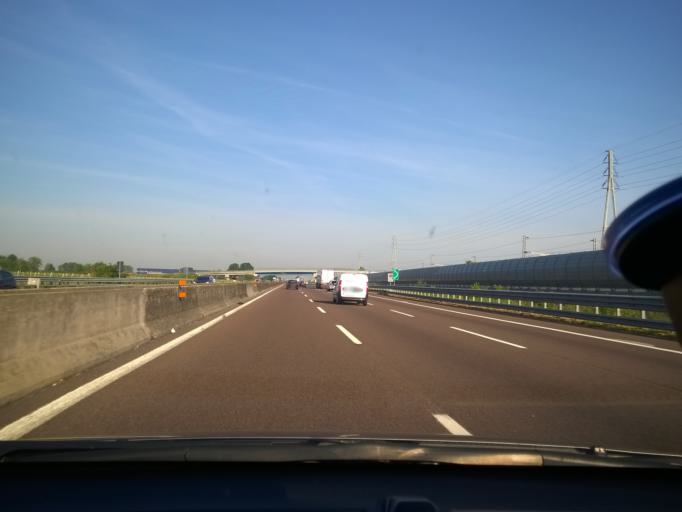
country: IT
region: Emilia-Romagna
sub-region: Provincia di Reggio Emilia
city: Rubiera
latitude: 44.6820
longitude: 10.8032
